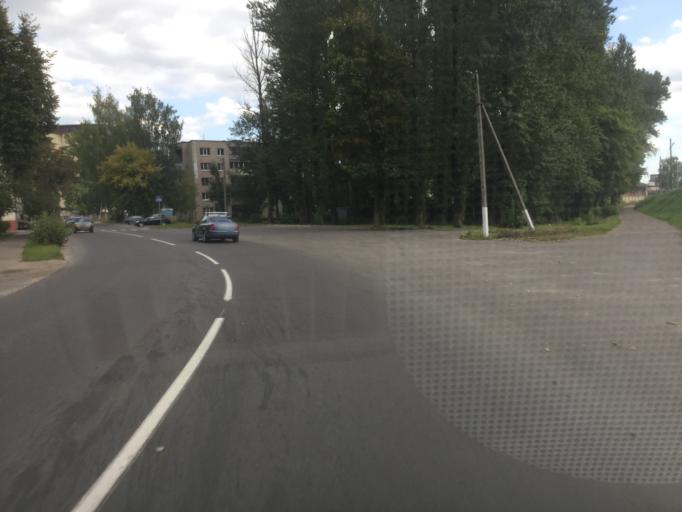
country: BY
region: Vitebsk
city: Vitebsk
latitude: 55.2034
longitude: 30.1850
